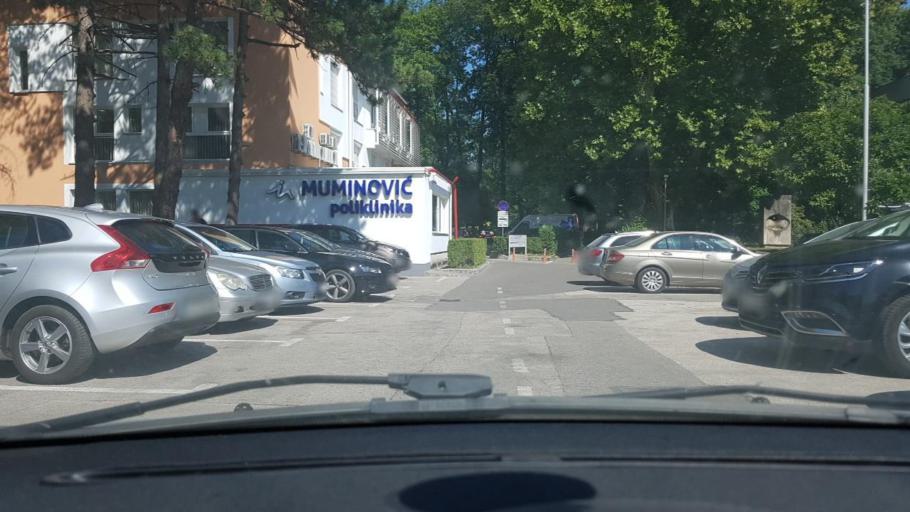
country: BA
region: Federation of Bosnia and Herzegovina
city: Bihac
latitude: 44.8128
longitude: 15.8690
